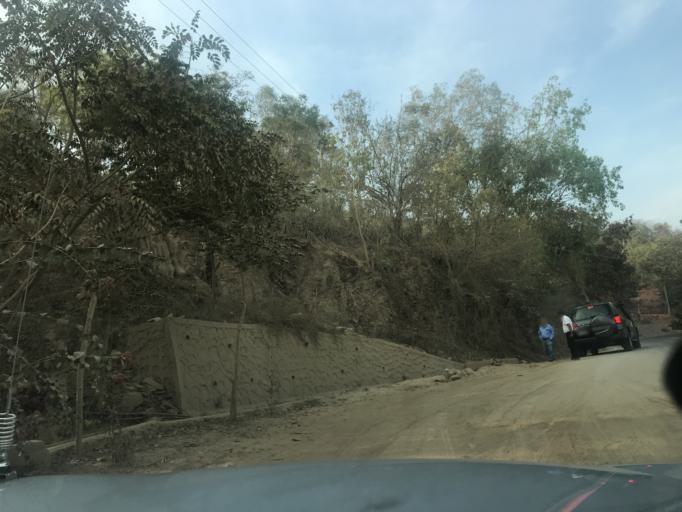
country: TL
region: Dili
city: Dili
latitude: -8.5733
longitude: 125.5876
